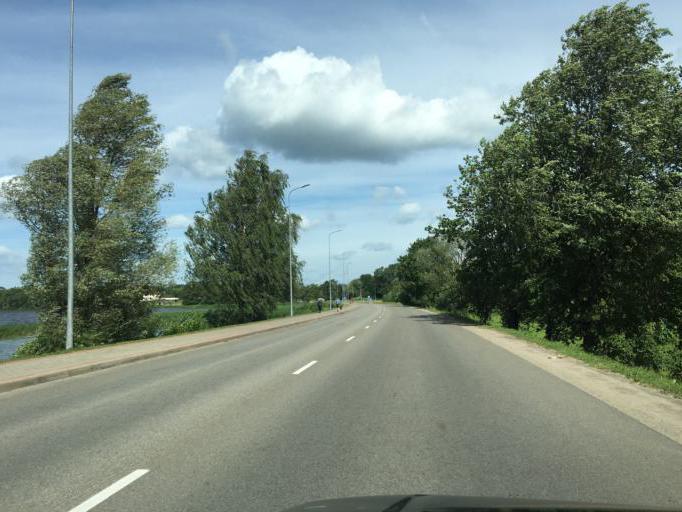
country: LV
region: Balvu Rajons
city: Balvi
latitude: 57.1353
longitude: 27.2605
